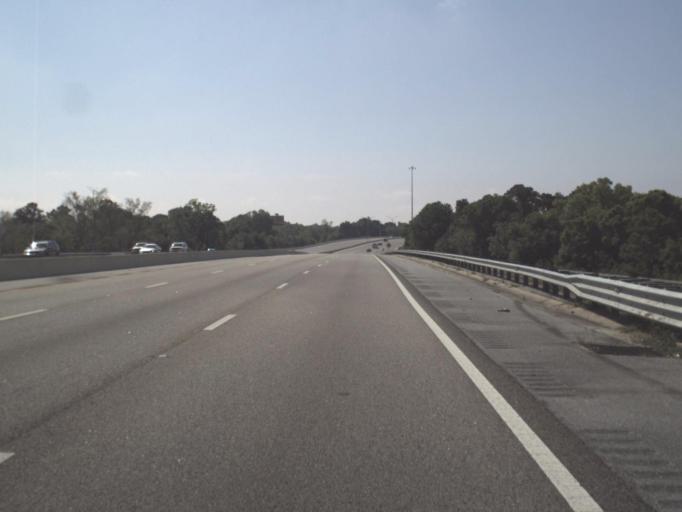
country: US
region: Florida
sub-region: Escambia County
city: Goulding
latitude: 30.4516
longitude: -87.2216
